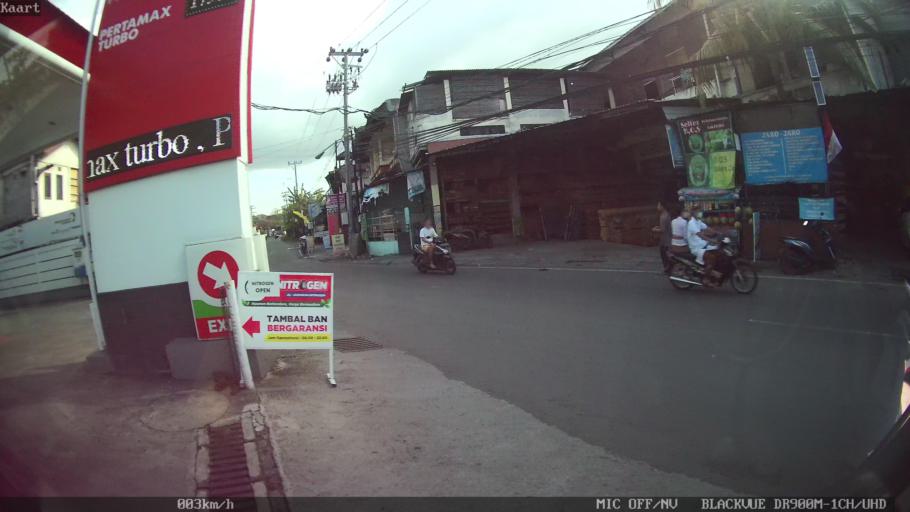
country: ID
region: Bali
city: Karyadharma
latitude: -8.6951
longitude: 115.1925
